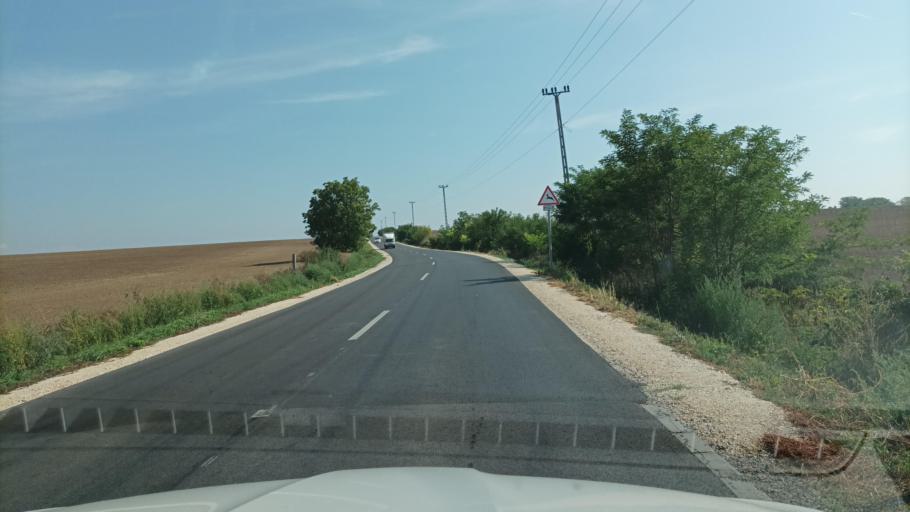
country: HU
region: Pest
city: Vacszentlaszlo
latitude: 47.5766
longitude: 19.5462
